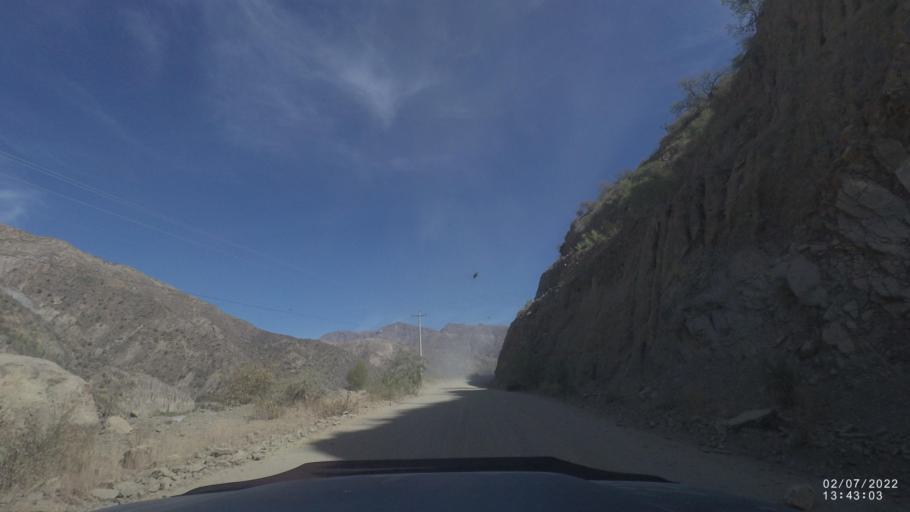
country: BO
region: Cochabamba
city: Irpa Irpa
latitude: -17.8032
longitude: -66.3580
